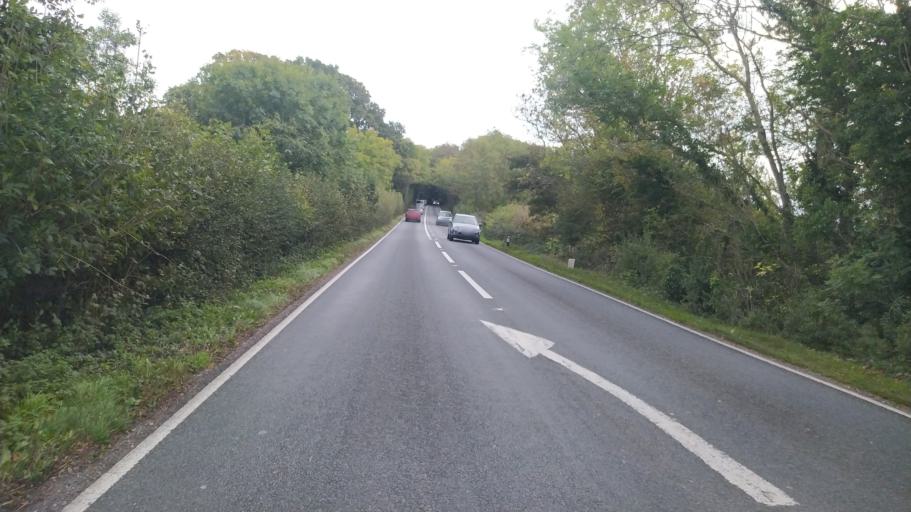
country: GB
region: England
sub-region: Dorset
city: Bovington Camp
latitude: 50.7488
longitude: -2.2084
